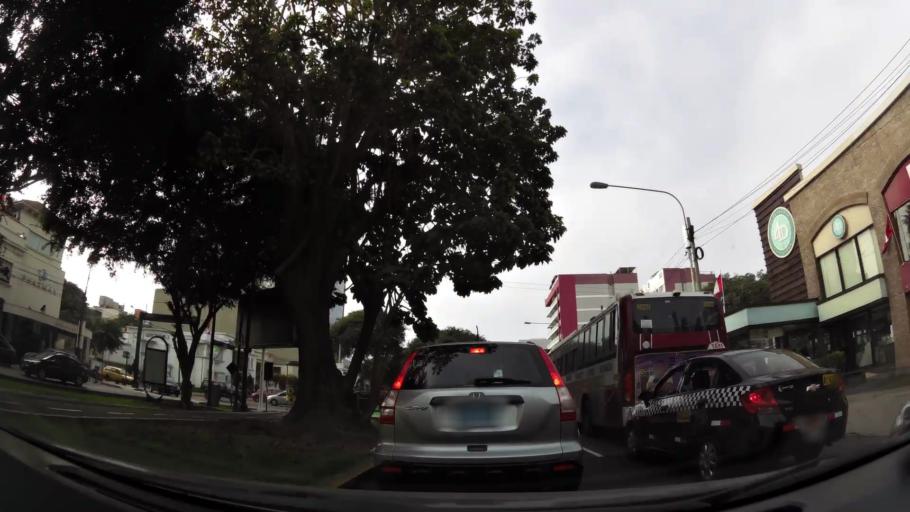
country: PE
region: Lima
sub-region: Lima
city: San Isidro
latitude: -12.0982
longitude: -77.0558
